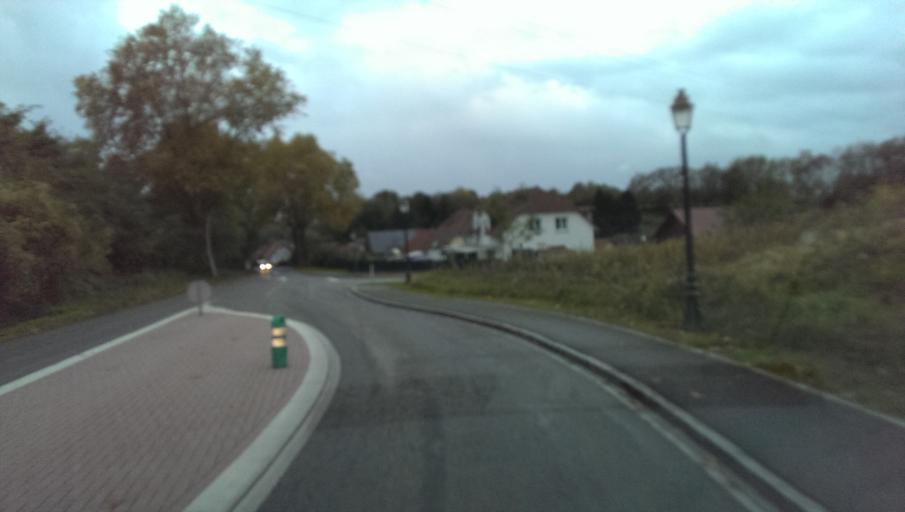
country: DE
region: Rheinland-Pfalz
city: Scheibenhardt
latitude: 48.9584
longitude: 8.1303
